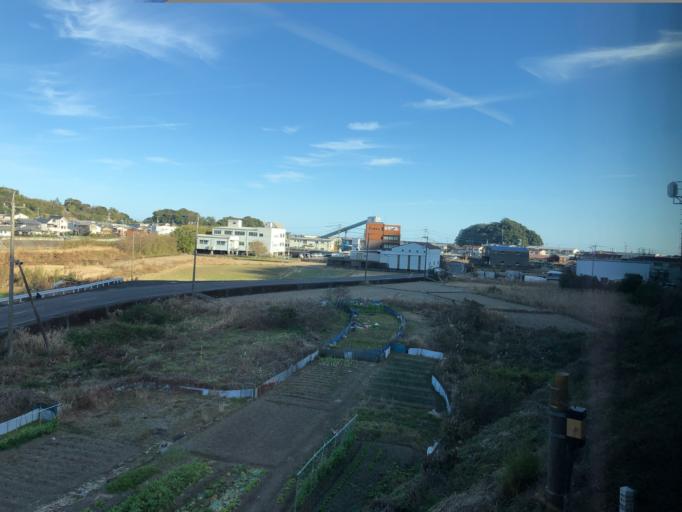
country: JP
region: Kochi
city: Nakamura
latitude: 33.0784
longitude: 133.1024
